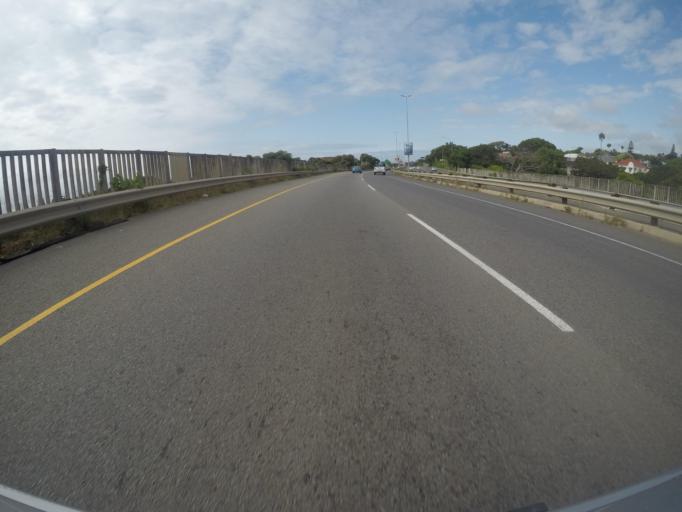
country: ZA
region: Eastern Cape
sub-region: Buffalo City Metropolitan Municipality
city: East London
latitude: -32.9893
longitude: 27.9195
